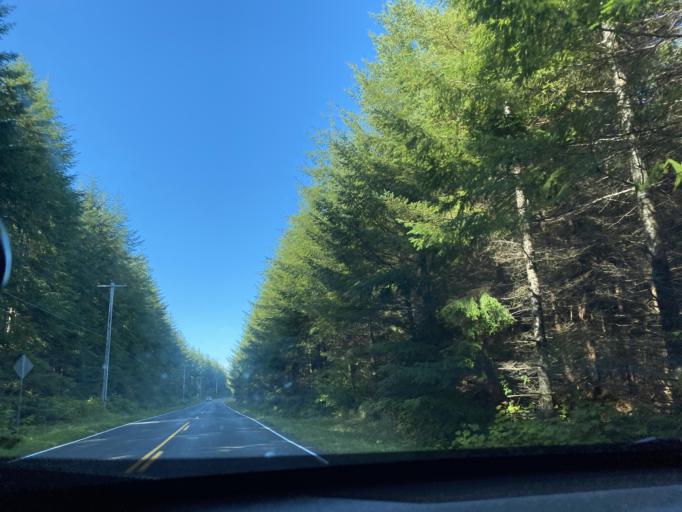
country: US
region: Washington
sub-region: Clallam County
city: Forks
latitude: 47.9471
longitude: -124.4896
